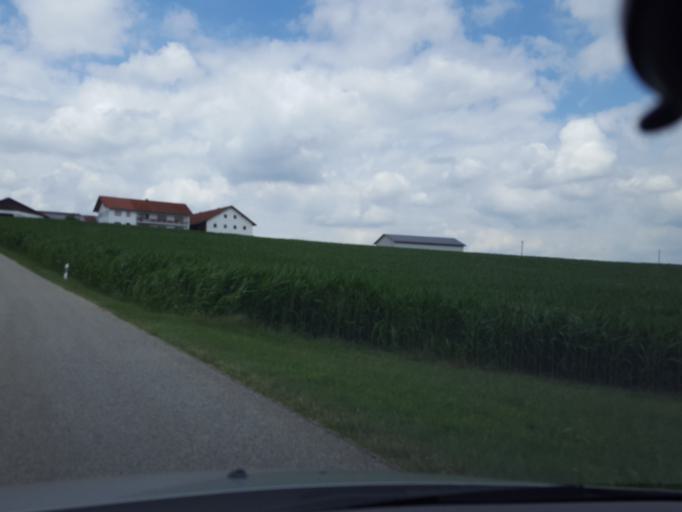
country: DE
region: Bavaria
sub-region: Upper Bavaria
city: Neumarkt-Sankt Veit
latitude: 48.3802
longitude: 12.4911
